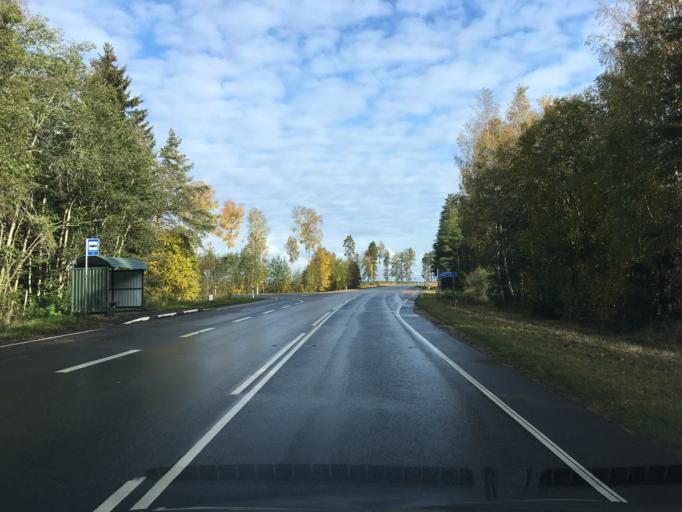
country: EE
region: Harju
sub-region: Raasiku vald
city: Raasiku
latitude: 59.2060
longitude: 25.1850
